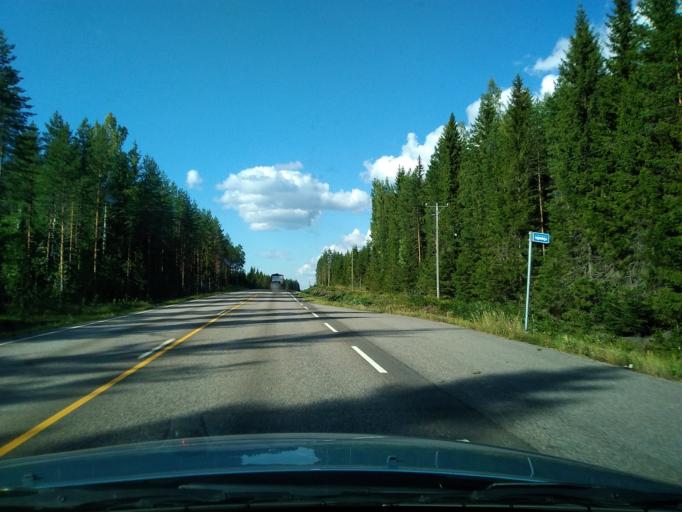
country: FI
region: Pirkanmaa
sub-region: Ylae-Pirkanmaa
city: Maenttae
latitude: 62.0768
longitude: 24.7250
